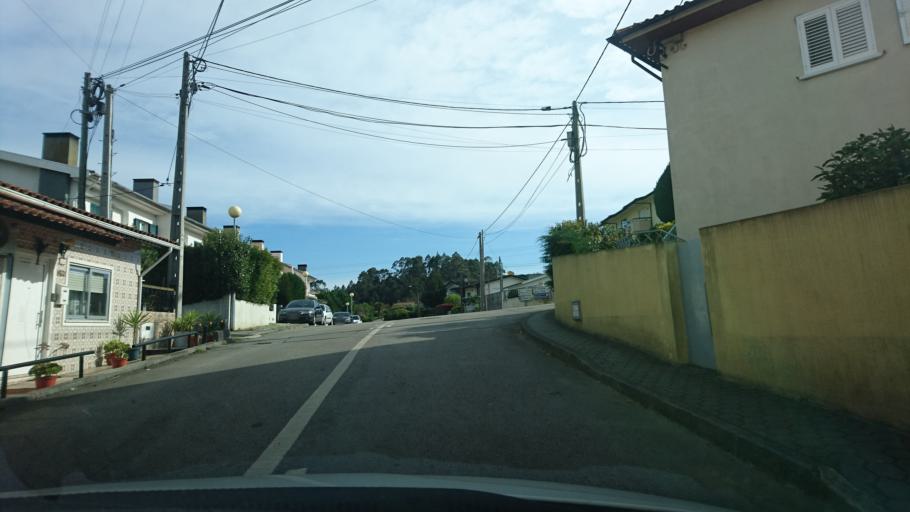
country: PT
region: Aveiro
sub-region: Oliveira de Azemeis
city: Sao Roque
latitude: 40.8773
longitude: -8.4851
